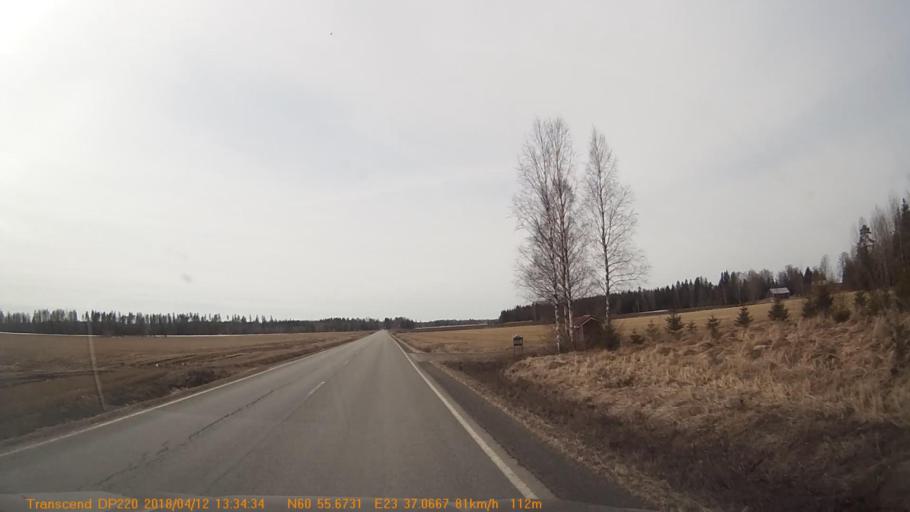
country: FI
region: Haeme
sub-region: Forssa
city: Forssa
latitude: 60.9278
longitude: 23.6173
